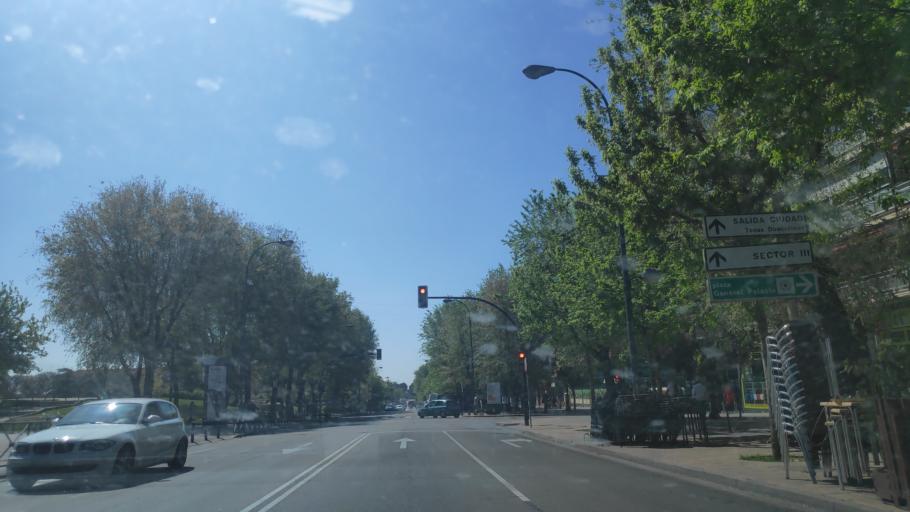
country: ES
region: Madrid
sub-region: Provincia de Madrid
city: Getafe
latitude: 40.3093
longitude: -3.7251
